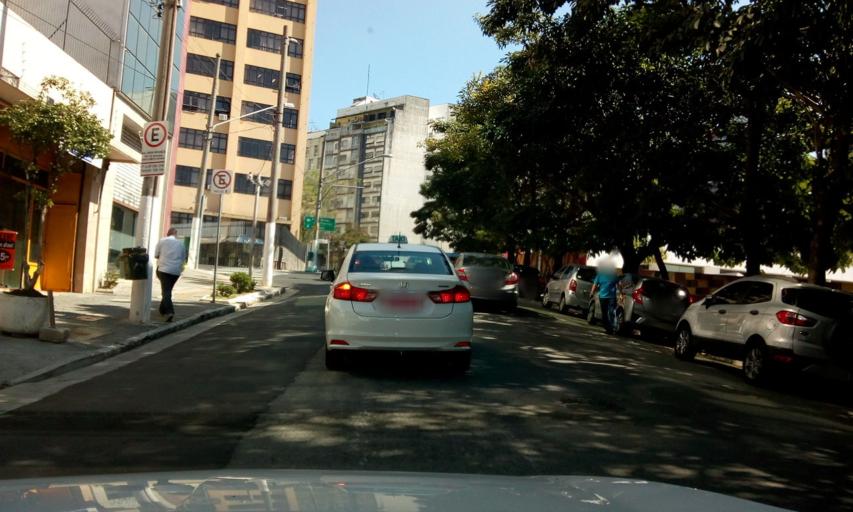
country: BR
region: Sao Paulo
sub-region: Sao Paulo
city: Sao Paulo
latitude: -23.5508
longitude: -46.6395
